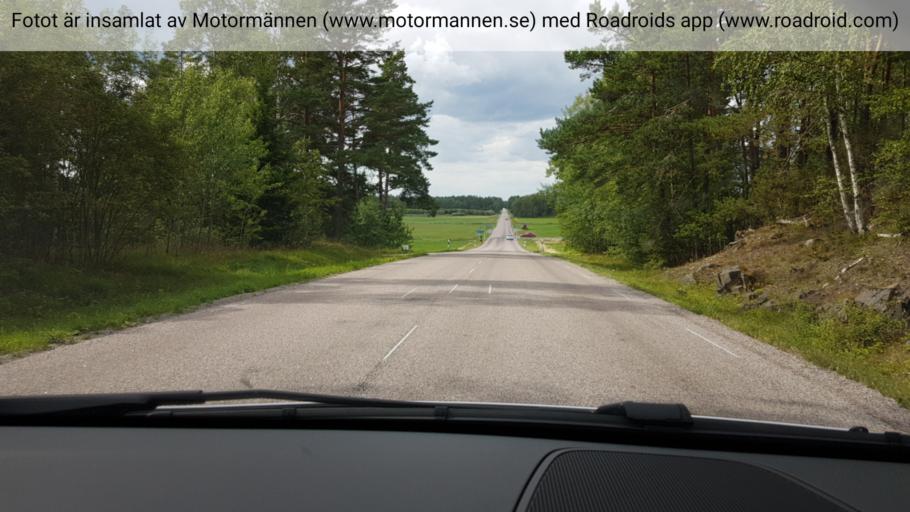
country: SE
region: Uppsala
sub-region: Osthammars Kommun
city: Gimo
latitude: 59.9585
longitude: 18.0835
